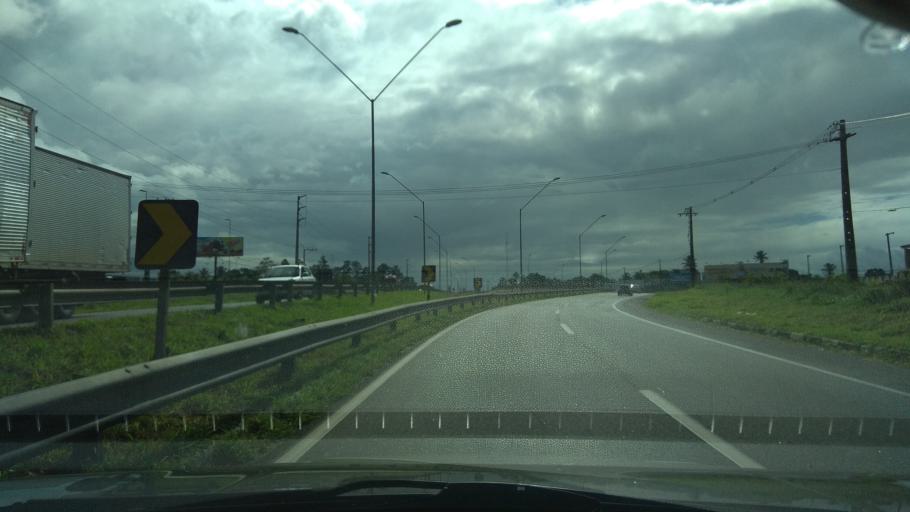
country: BR
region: Bahia
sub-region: Conceicao Do Jacuipe
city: Conceicao do Jacuipe
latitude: -12.3207
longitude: -38.8713
